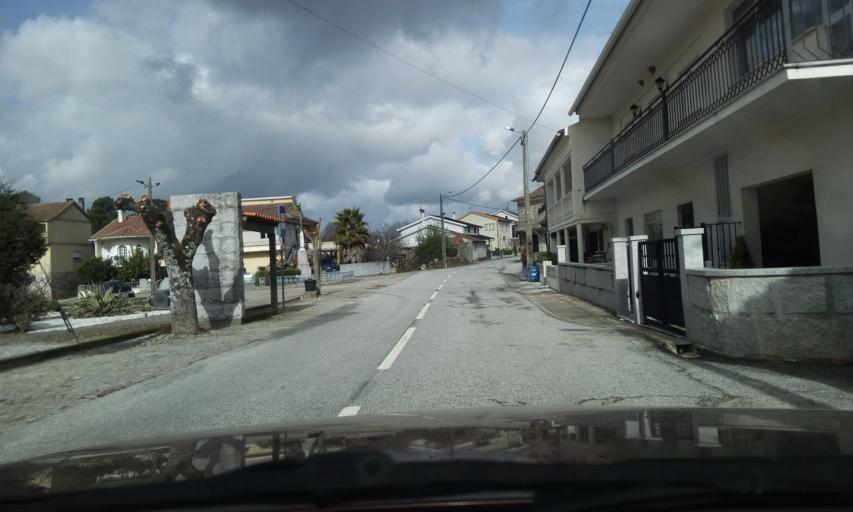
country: PT
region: Guarda
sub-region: Fornos de Algodres
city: Fornos de Algodres
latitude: 40.6501
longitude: -7.5477
